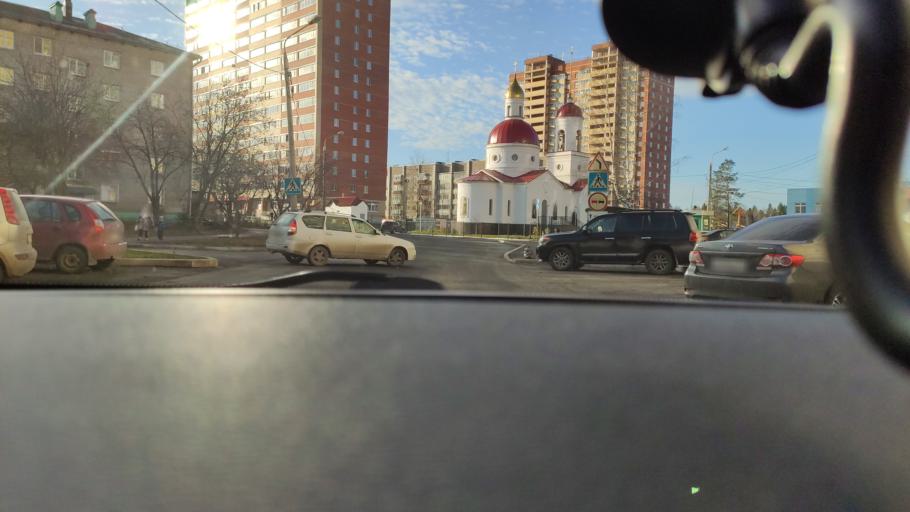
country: RU
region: Perm
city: Kondratovo
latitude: 58.0491
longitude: 56.0879
